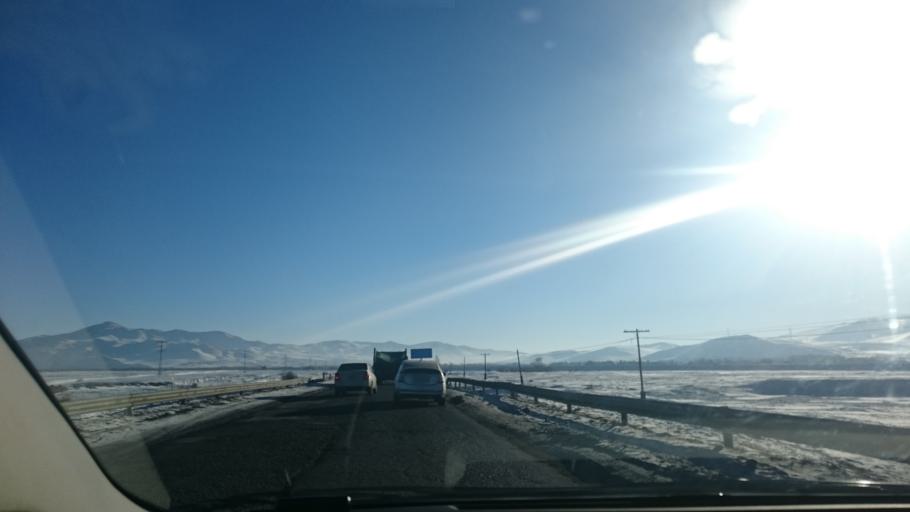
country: MN
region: Ulaanbaatar
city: Ulaanbaatar
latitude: 47.8998
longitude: 107.0375
